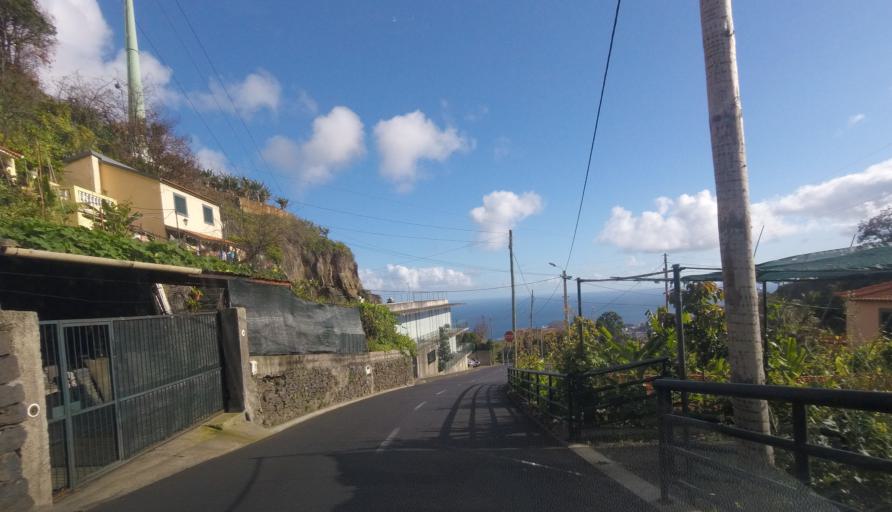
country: PT
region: Madeira
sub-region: Funchal
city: Nossa Senhora do Monte
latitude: 32.6663
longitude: -16.9012
